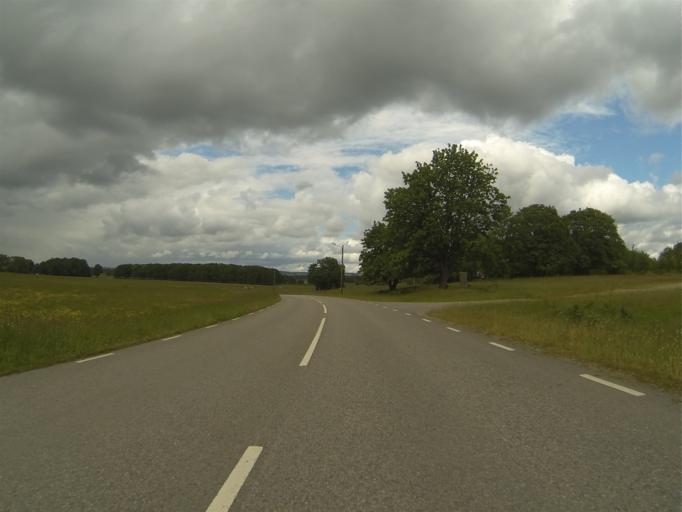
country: SE
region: Skane
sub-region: Lunds Kommun
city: Veberod
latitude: 55.6967
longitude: 13.4226
